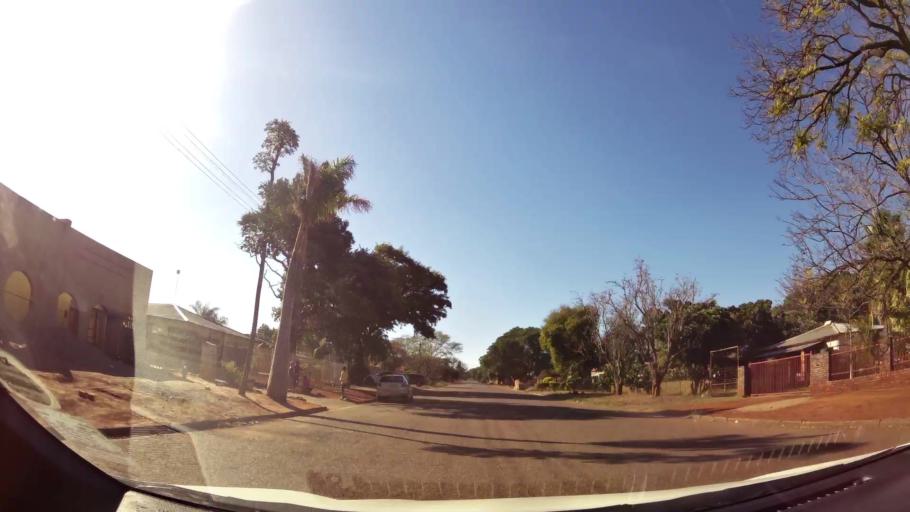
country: ZA
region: Limpopo
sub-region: Waterberg District Municipality
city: Mokopane
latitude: -24.1904
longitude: 29.0014
